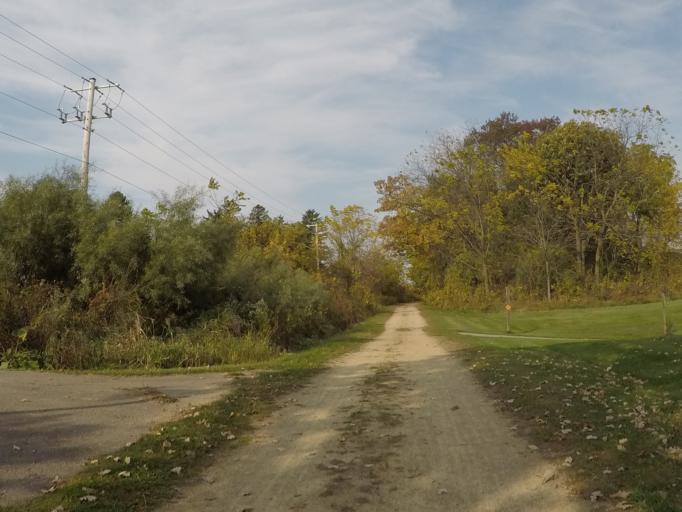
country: US
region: Wisconsin
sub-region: Iowa County
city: Barneveld
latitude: 43.0143
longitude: -89.8233
